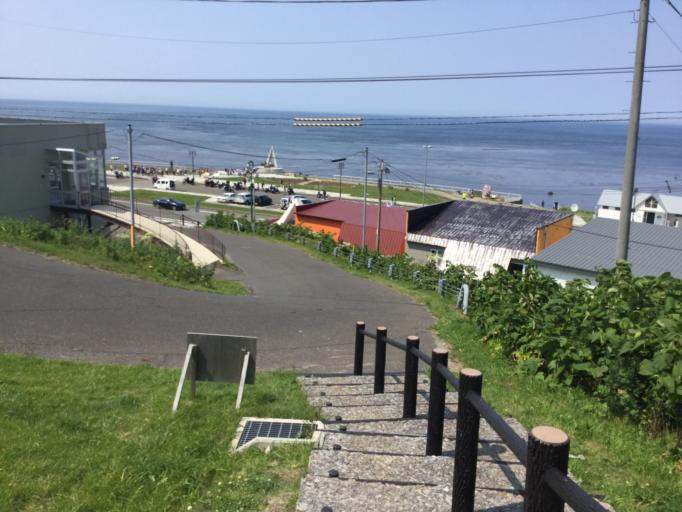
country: JP
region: Hokkaido
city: Makubetsu
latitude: 45.5216
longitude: 141.9375
